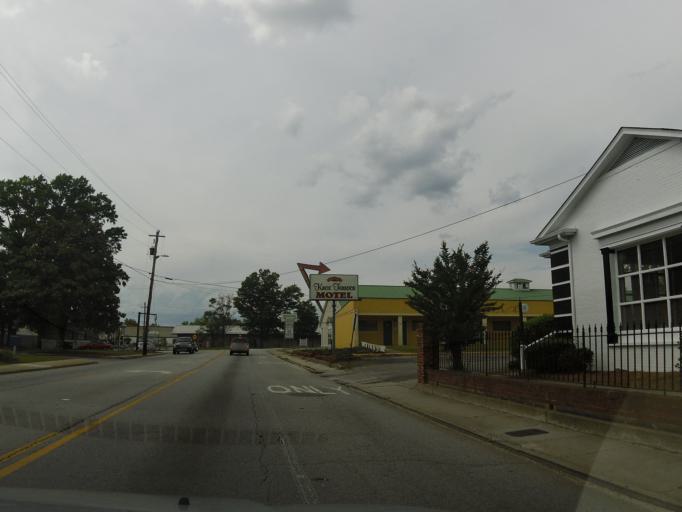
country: US
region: Georgia
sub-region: McDuffie County
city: Thomson
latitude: 33.4647
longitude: -82.5013
